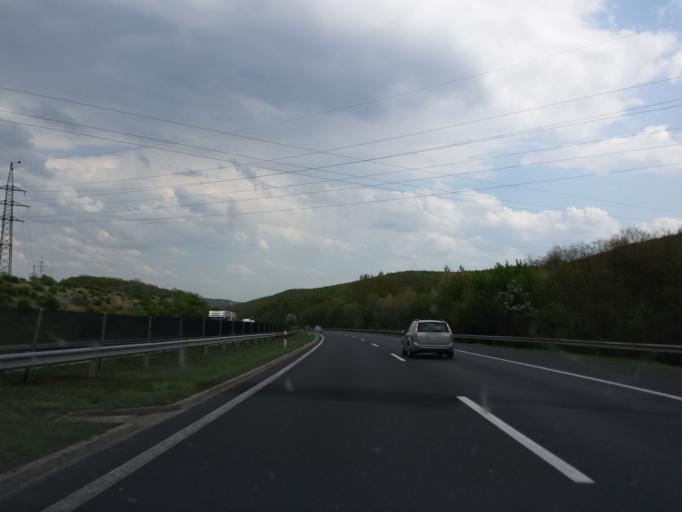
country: HU
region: Fejer
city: Szarliget
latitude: 47.5255
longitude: 18.5067
